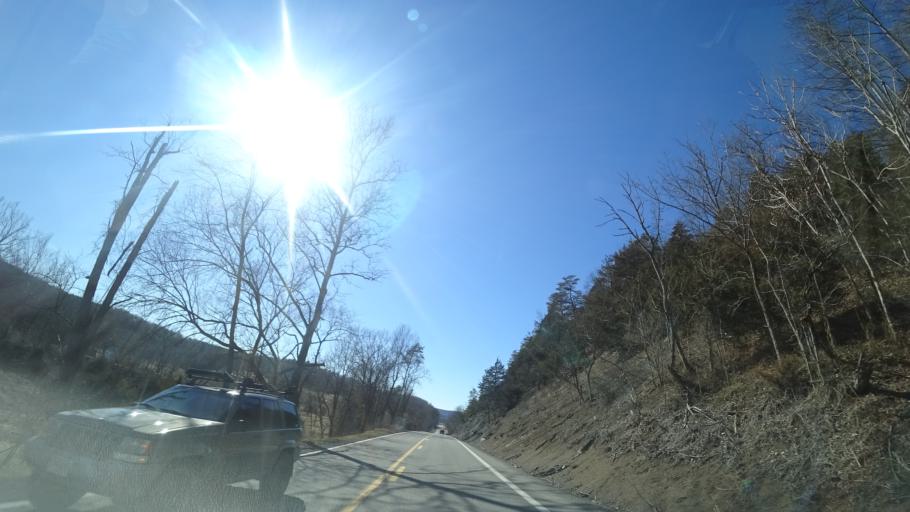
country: US
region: Virginia
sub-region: Shenandoah County
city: Woodstock
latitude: 39.0951
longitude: -78.5655
